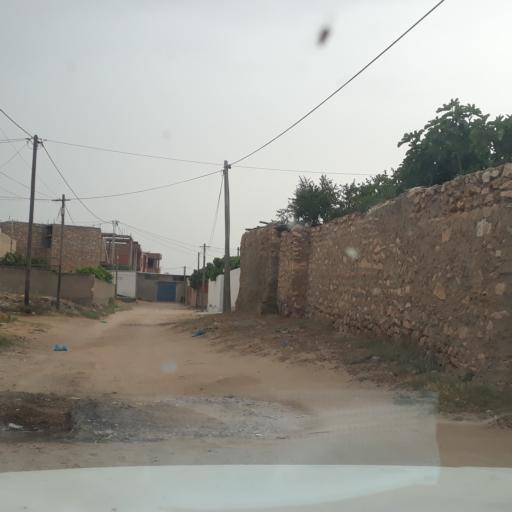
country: TN
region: Safaqis
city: Al Qarmadah
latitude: 34.8265
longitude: 10.7767
